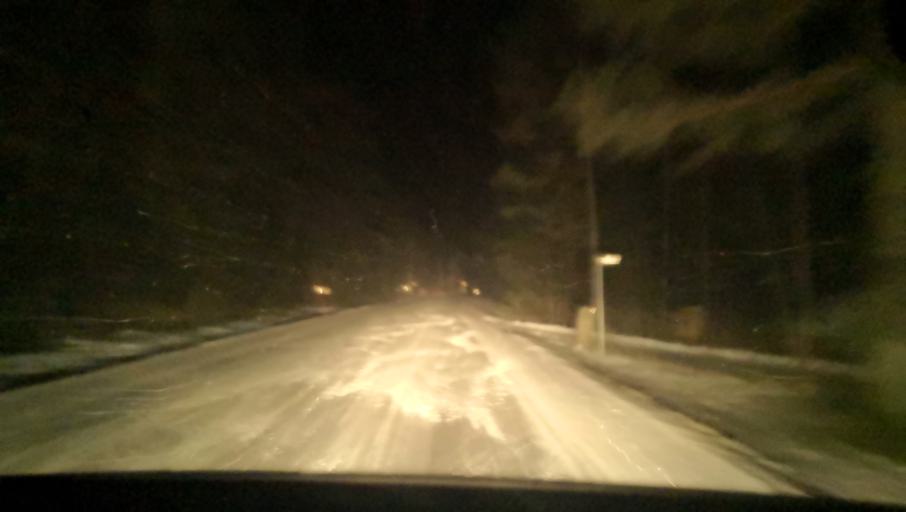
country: SE
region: Uppsala
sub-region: Heby Kommun
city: Tarnsjo
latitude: 60.1414
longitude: 16.9085
